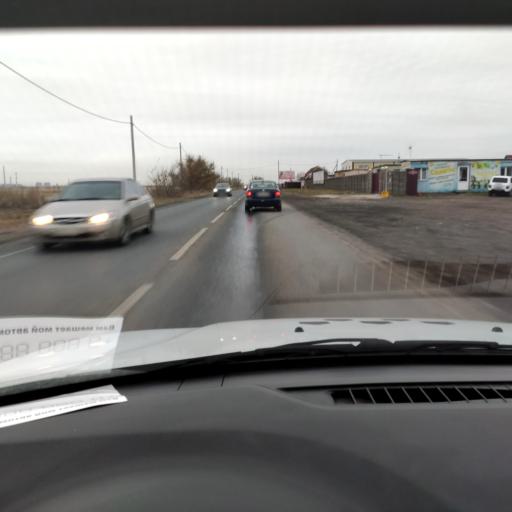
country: RU
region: Samara
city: Podstepki
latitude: 53.5182
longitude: 49.2201
